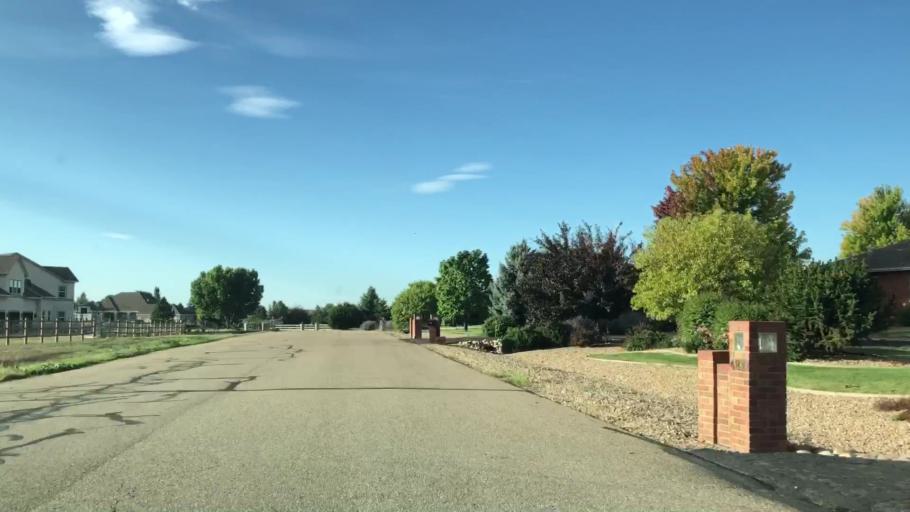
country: US
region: Colorado
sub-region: Weld County
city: Windsor
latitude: 40.4430
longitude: -104.9494
